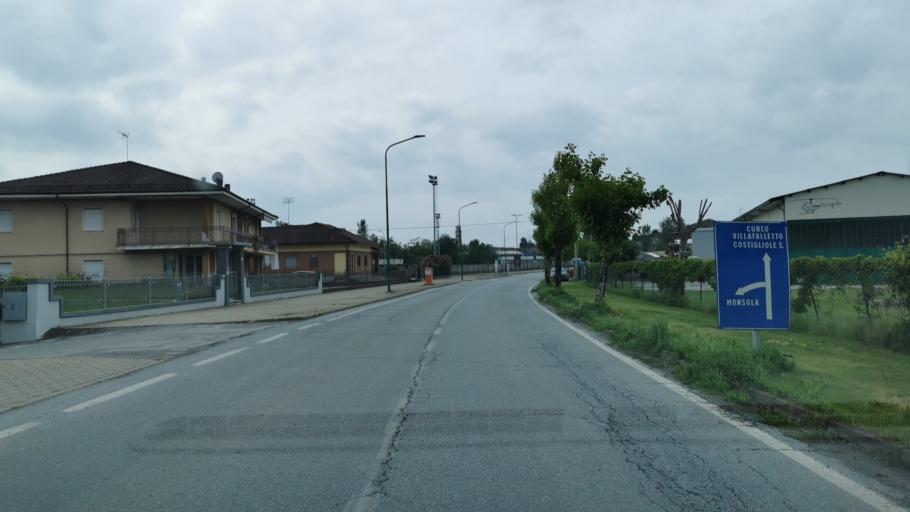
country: IT
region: Piedmont
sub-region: Provincia di Cuneo
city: Villafalletto
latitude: 44.5513
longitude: 7.5398
